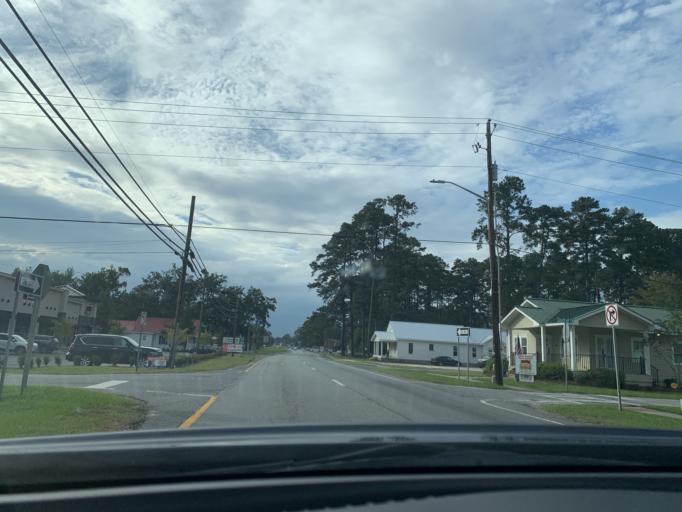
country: US
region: Georgia
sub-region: Chatham County
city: Pooler
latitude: 32.1173
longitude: -81.2524
